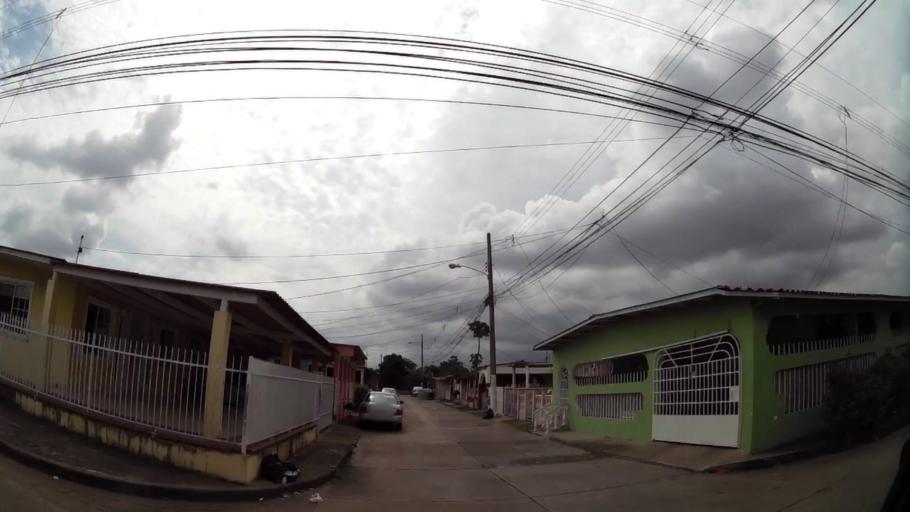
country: PA
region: Panama
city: Tocumen
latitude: 9.0495
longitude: -79.4161
